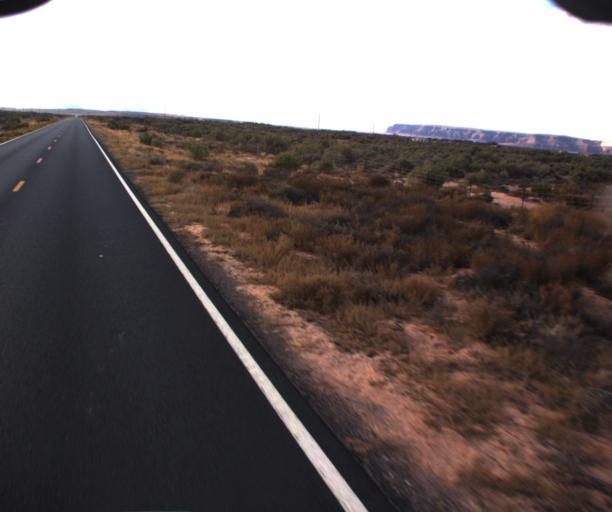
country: US
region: Arizona
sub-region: Apache County
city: Many Farms
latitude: 36.6431
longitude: -109.5895
